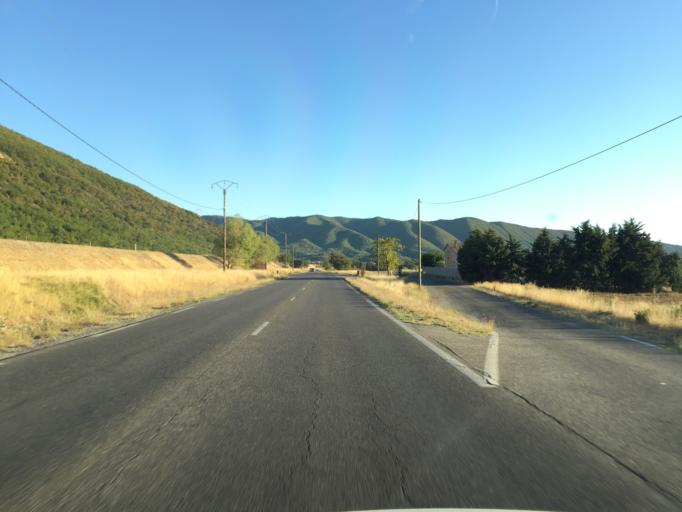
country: FR
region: Provence-Alpes-Cote d'Azur
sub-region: Departement des Alpes-de-Haute-Provence
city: Malijai
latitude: 44.0657
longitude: 6.0216
